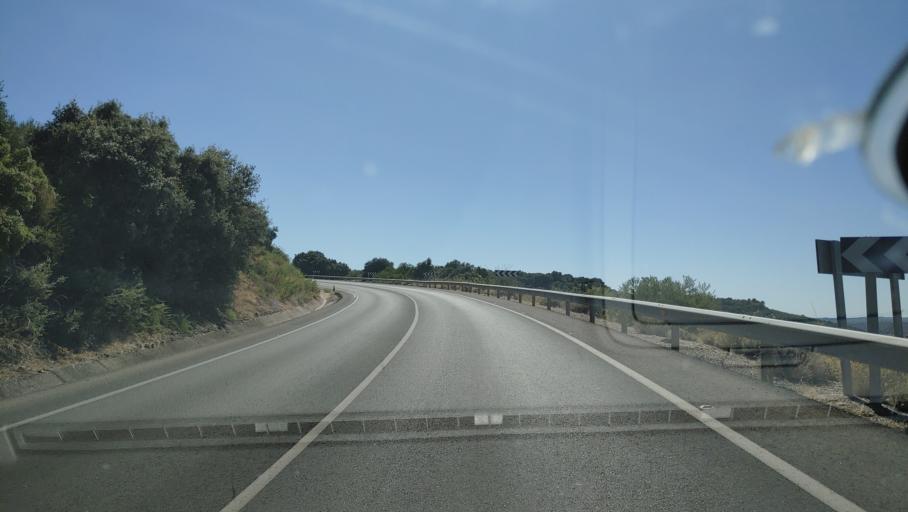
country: ES
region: Andalusia
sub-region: Provincia de Jaen
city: Campina
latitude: 38.2351
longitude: -2.9714
